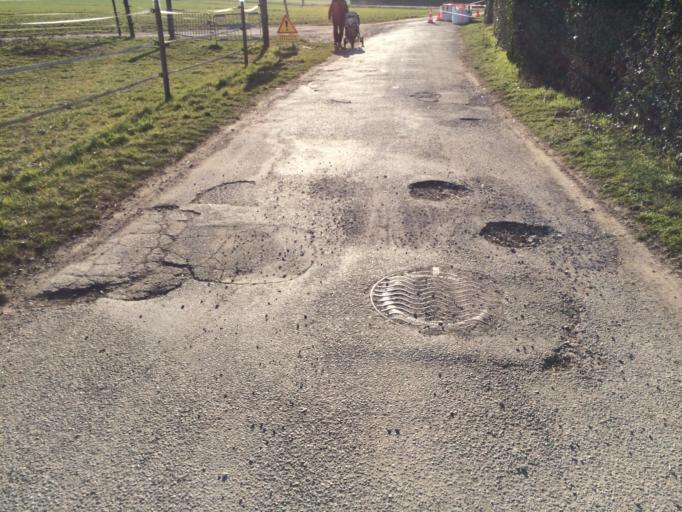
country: FR
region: Ile-de-France
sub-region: Departement de l'Essonne
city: Vauhallan
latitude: 48.7277
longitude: 2.2107
